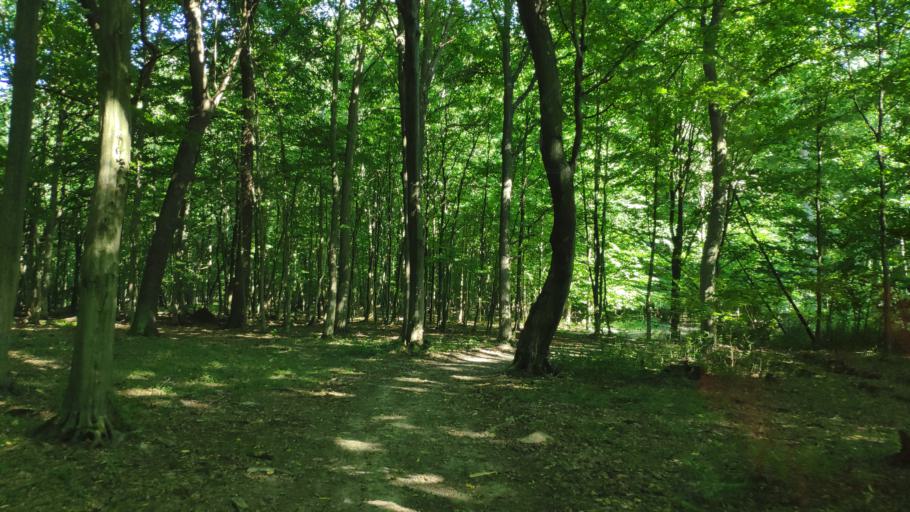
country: SK
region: Presovsky
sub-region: Okres Presov
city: Presov
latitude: 48.9062
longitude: 21.2913
